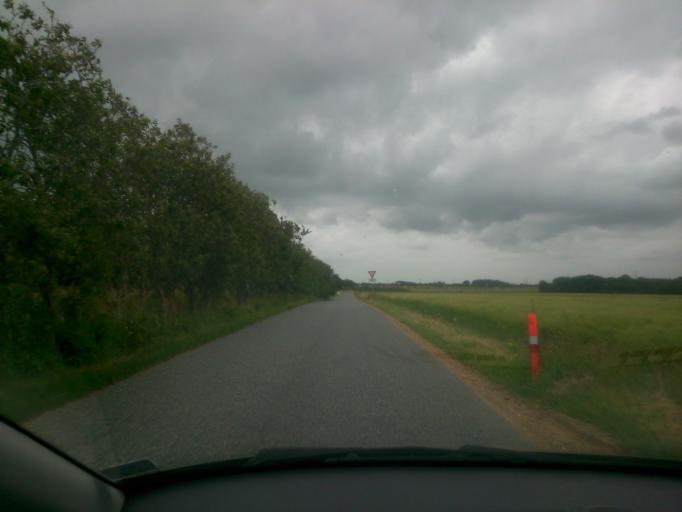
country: DK
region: South Denmark
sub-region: Esbjerg Kommune
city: Esbjerg
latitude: 55.5435
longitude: 8.4611
